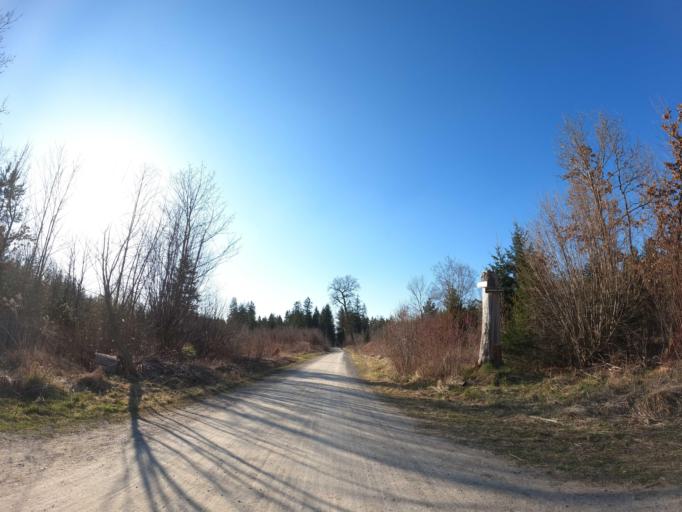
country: DE
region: Bavaria
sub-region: Upper Bavaria
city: Unterhaching
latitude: 48.0706
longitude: 11.5886
